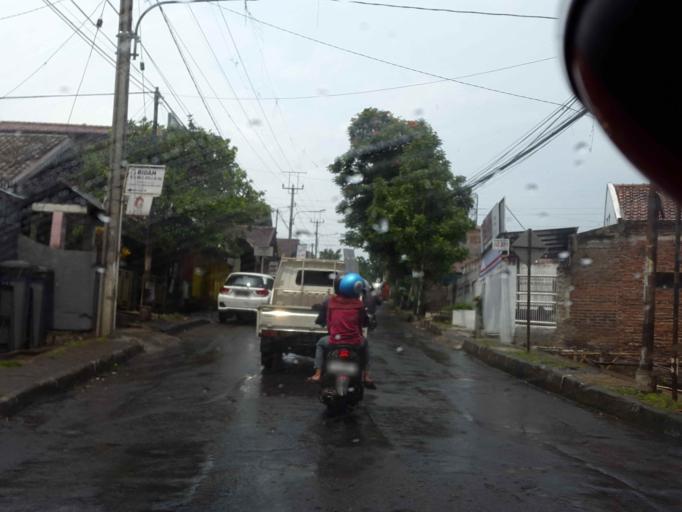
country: ID
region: West Java
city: Cimahi
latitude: -6.8674
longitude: 107.5429
